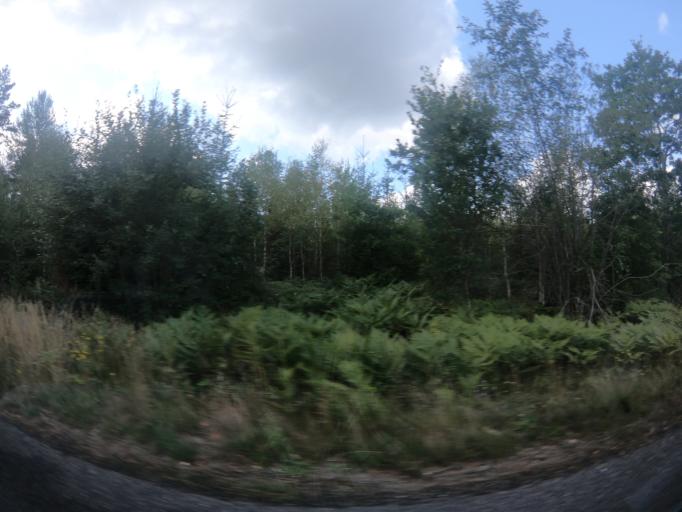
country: SE
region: Kronoberg
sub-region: Vaxjo Kommun
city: Braas
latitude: 57.0823
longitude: 15.0015
